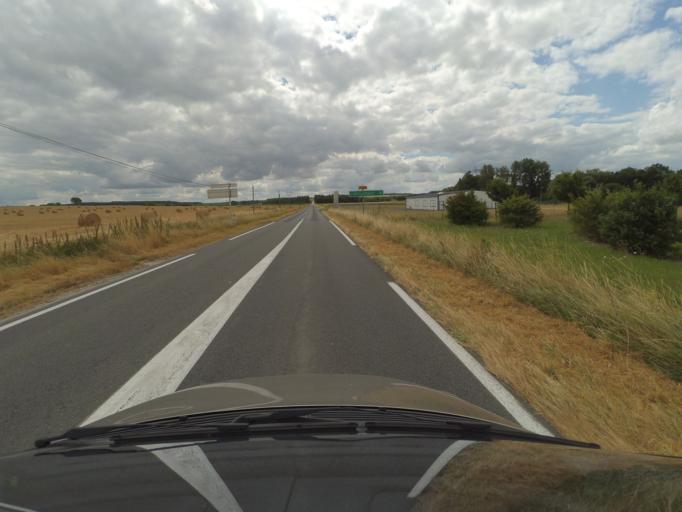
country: FR
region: Poitou-Charentes
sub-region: Departement de la Vienne
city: Saint-Gervais-les-Trois-Clochers
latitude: 46.9428
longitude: 0.4192
